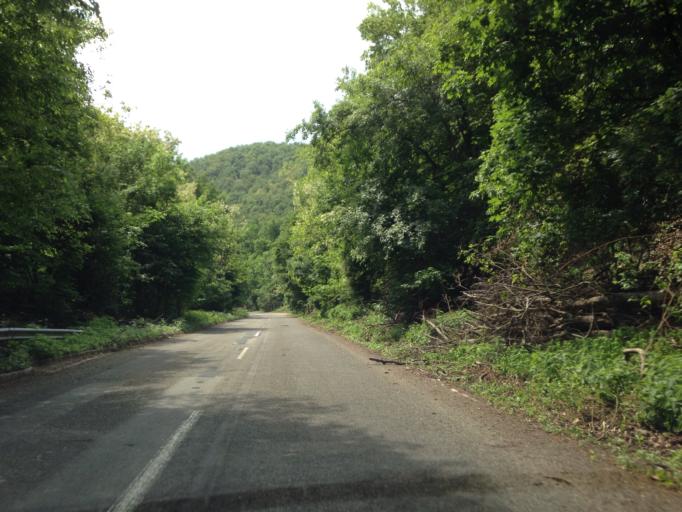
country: HU
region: Pest
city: Visegrad
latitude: 47.7567
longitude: 18.9464
